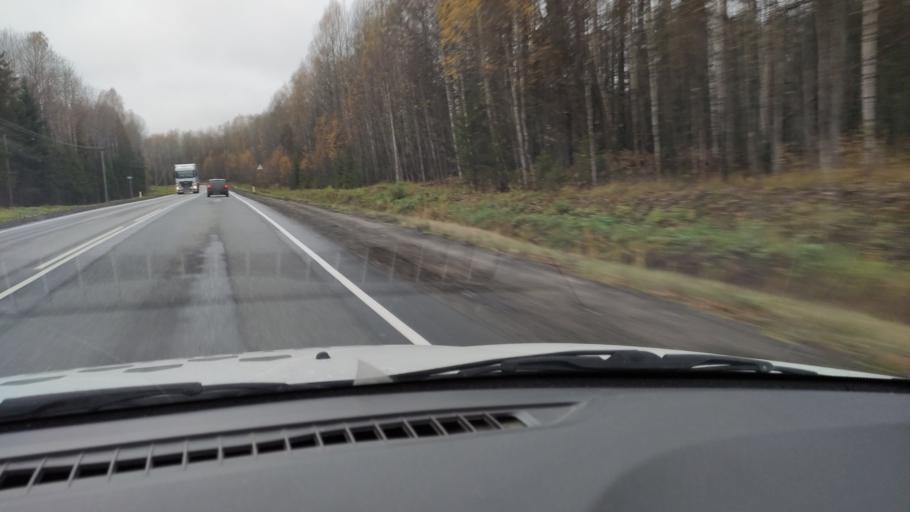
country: RU
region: Kirov
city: Belaya Kholunitsa
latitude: 58.9209
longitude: 51.1181
